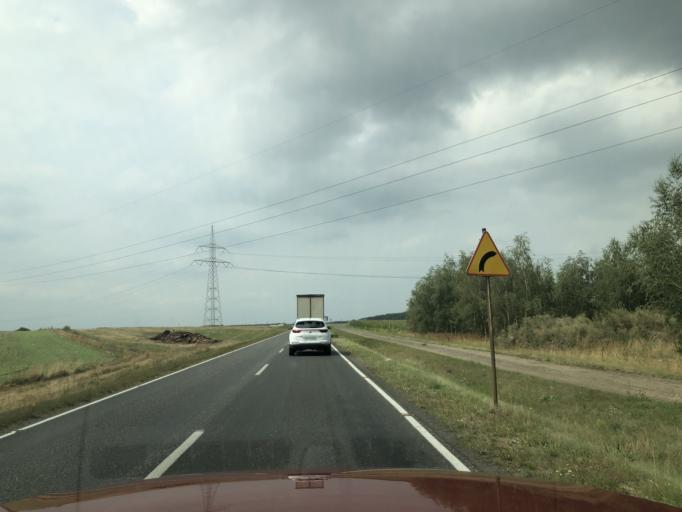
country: PL
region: Greater Poland Voivodeship
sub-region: Powiat leszczynski
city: Swieciechowa
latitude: 51.8614
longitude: 16.4916
